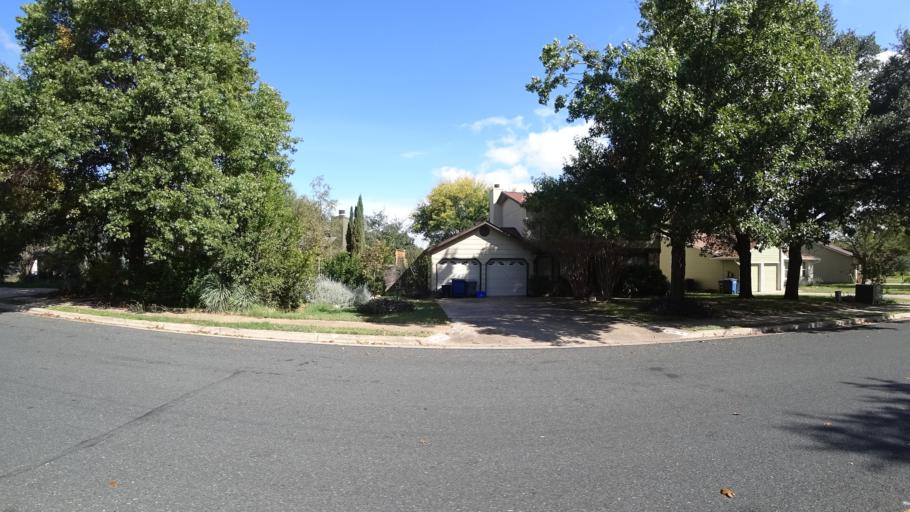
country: US
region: Texas
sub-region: Travis County
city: Wells Branch
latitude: 30.4249
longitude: -97.7241
